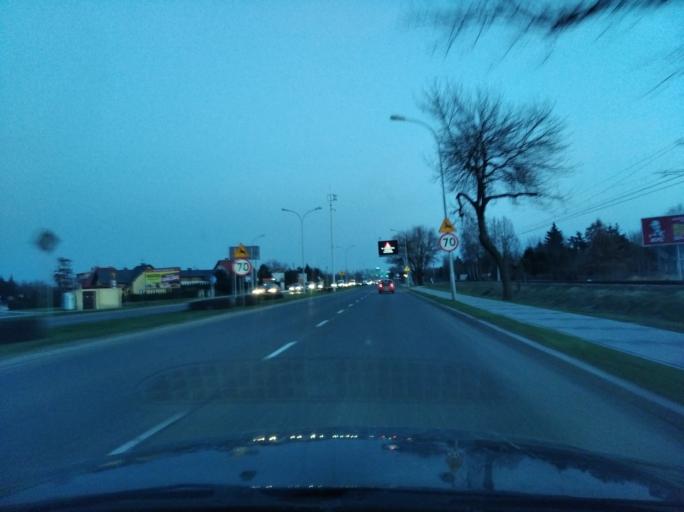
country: PL
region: Subcarpathian Voivodeship
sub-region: Rzeszow
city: Rzeszow
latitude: 50.0695
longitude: 21.9900
